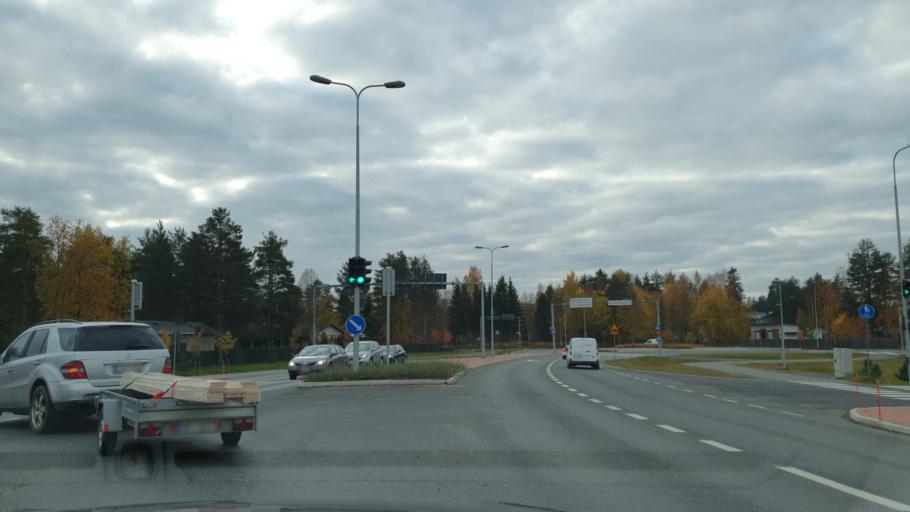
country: FI
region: Lapland
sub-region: Rovaniemi
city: Rovaniemi
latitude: 66.4900
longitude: 25.6924
